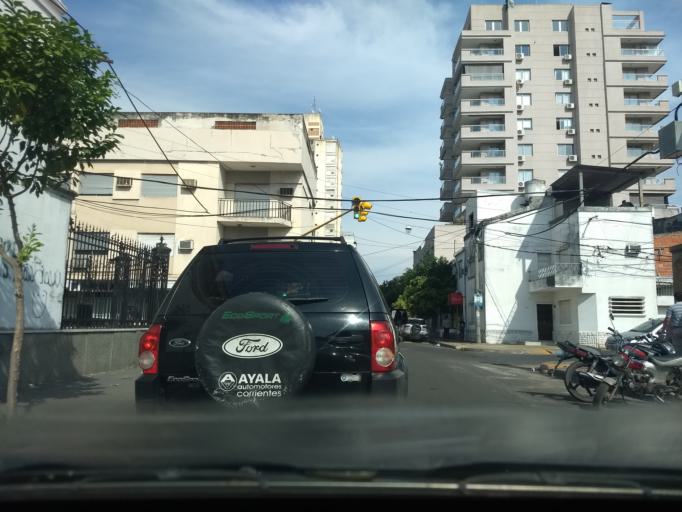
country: AR
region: Corrientes
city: Corrientes
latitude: -27.4668
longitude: -58.8303
